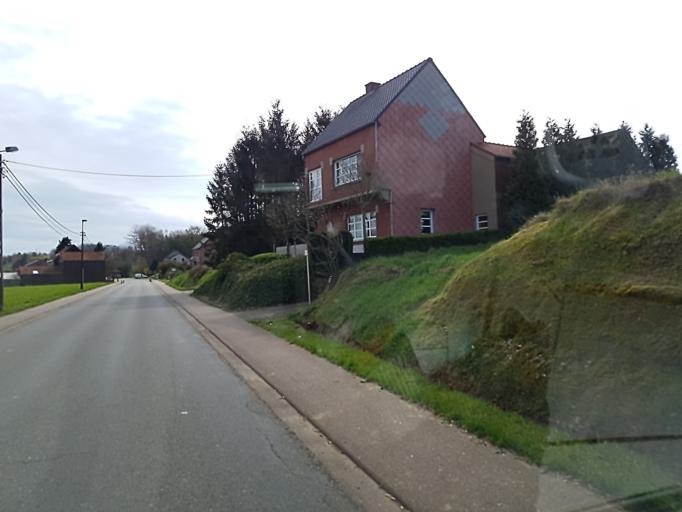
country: BE
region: Flanders
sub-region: Provincie Vlaams-Brabant
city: Diest
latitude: 50.9852
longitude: 5.0250
